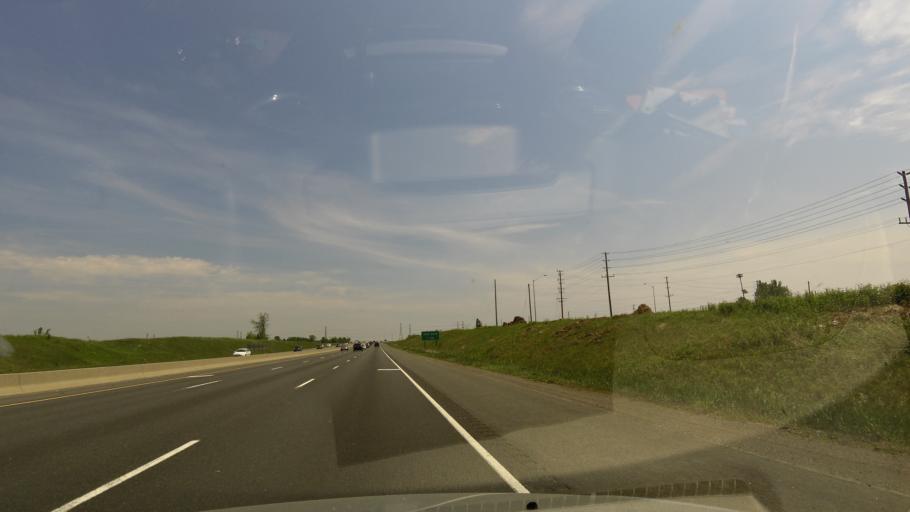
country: CA
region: Ontario
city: Oshawa
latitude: 43.8810
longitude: -78.7446
